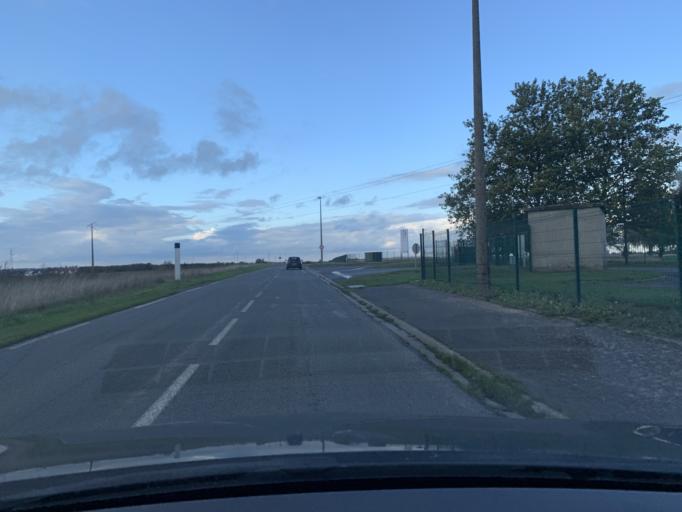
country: FR
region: Nord-Pas-de-Calais
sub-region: Departement du Nord
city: Proville
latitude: 50.1481
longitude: 3.2105
